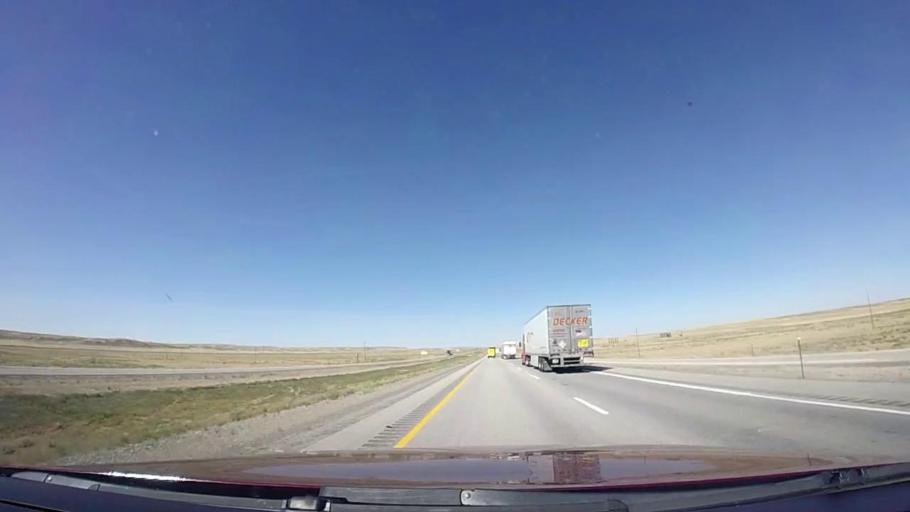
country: US
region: Wyoming
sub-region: Carbon County
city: Rawlins
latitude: 41.6650
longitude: -108.0360
